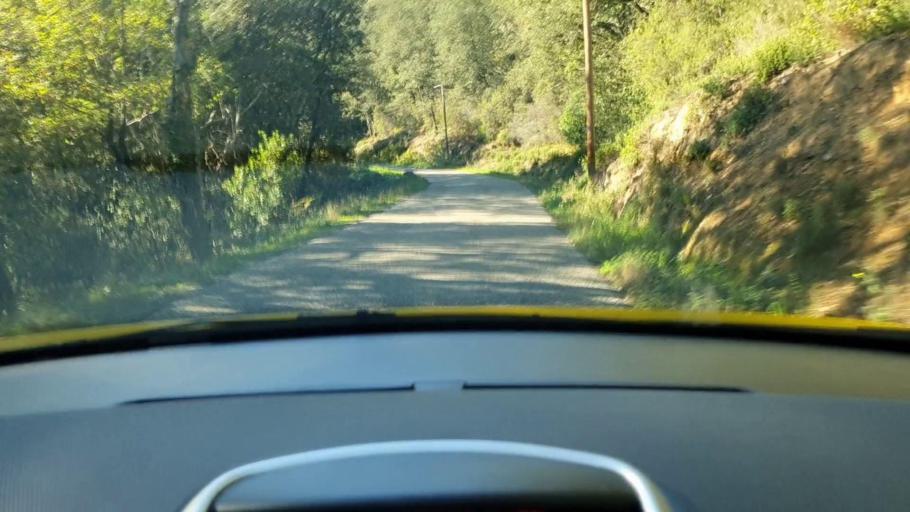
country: FR
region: Languedoc-Roussillon
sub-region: Departement du Gard
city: Sumene
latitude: 43.9833
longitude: 3.6814
